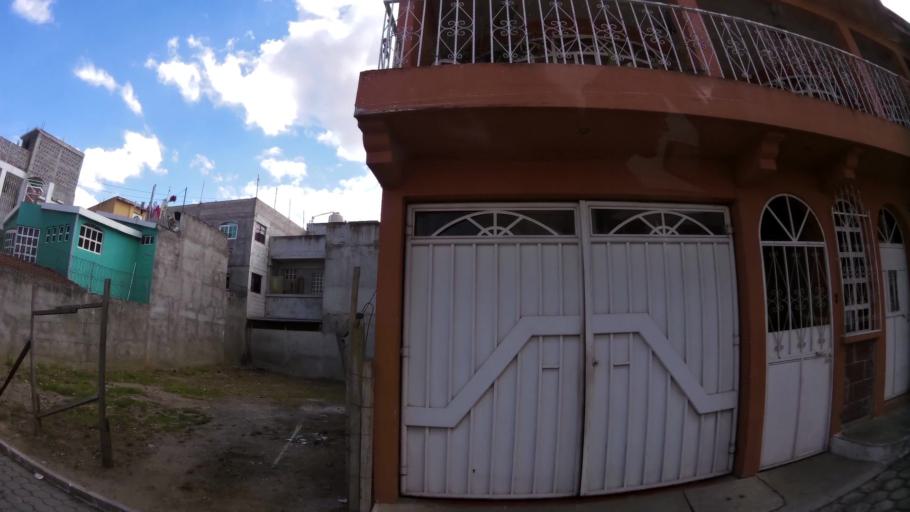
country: GT
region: Quetzaltenango
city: Quetzaltenango
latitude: 14.8471
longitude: -91.5406
